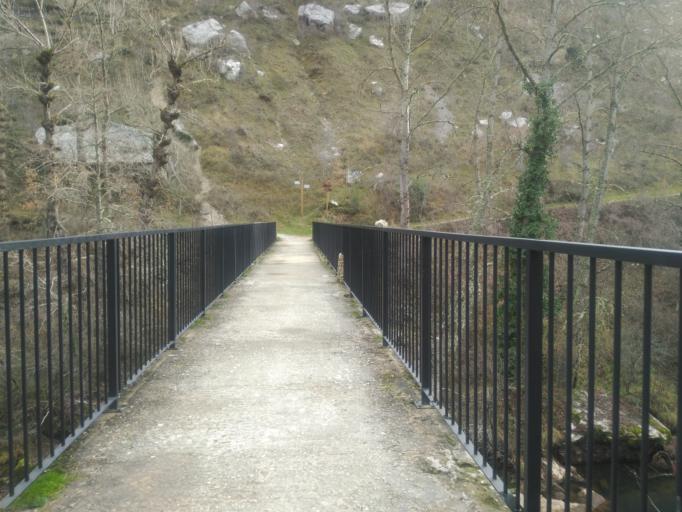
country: ES
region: Cantabria
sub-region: Provincia de Cantabria
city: San Martin de Elines
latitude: 42.8329
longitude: -3.7920
